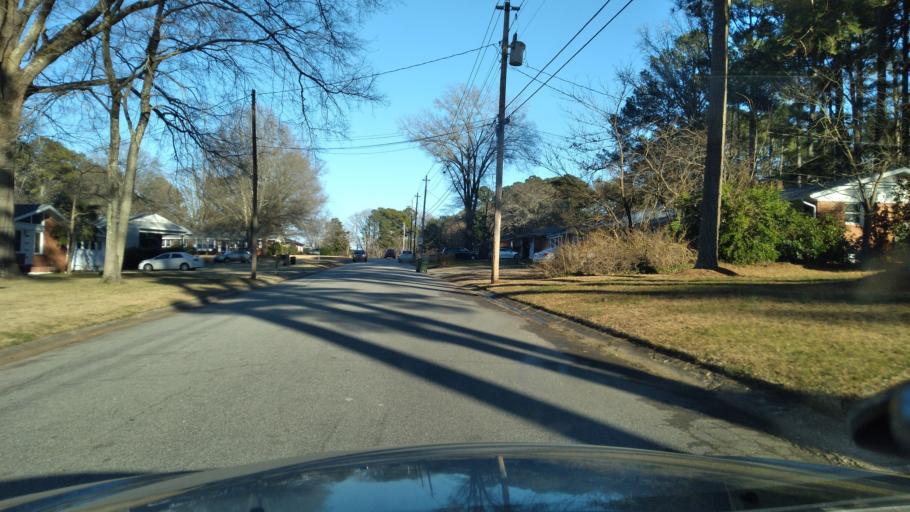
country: US
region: North Carolina
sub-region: Wake County
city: Garner
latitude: 35.6971
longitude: -78.6241
